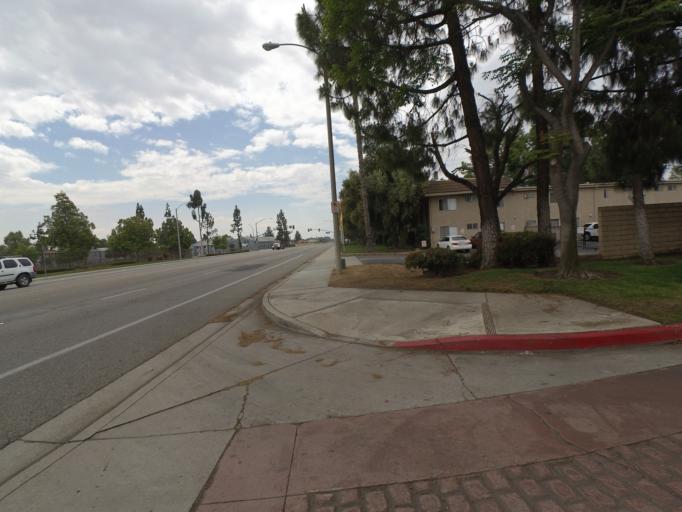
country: US
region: California
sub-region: Riverside County
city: Moreno Valley
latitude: 33.9292
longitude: -117.2440
